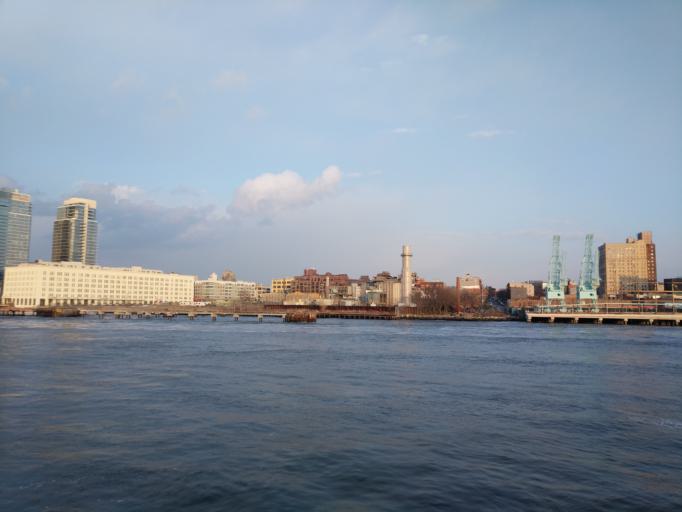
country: US
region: New York
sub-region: Queens County
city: Long Island City
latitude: 40.7174
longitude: -73.9699
